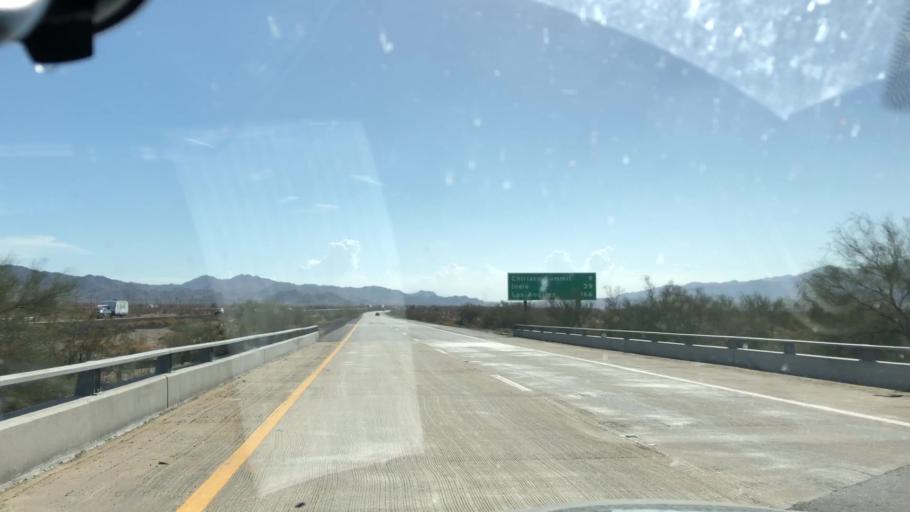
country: US
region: California
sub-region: Imperial County
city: Niland
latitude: 33.6753
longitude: -115.5743
